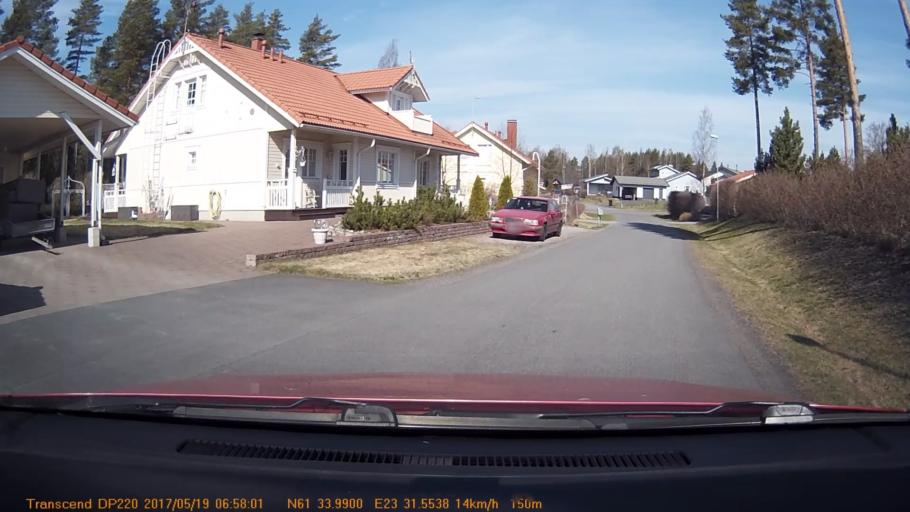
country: FI
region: Pirkanmaa
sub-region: Tampere
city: Yloejaervi
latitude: 61.5666
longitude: 23.5260
